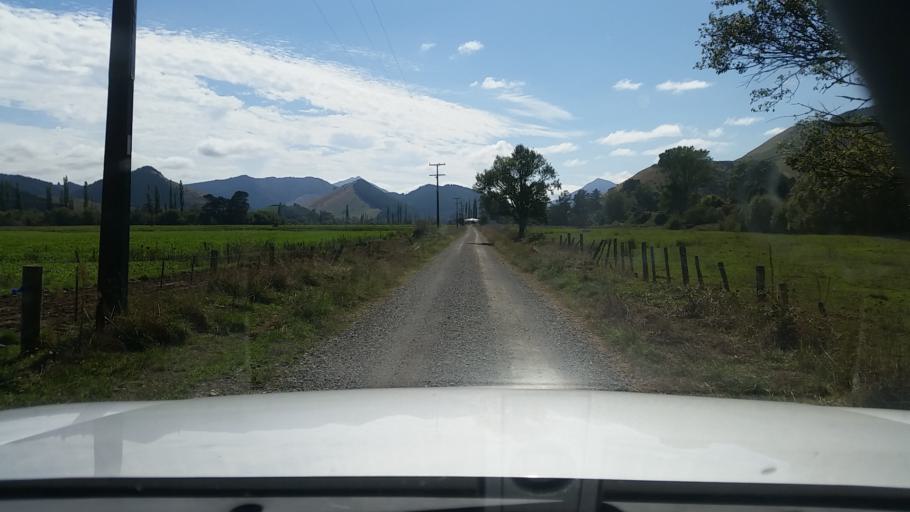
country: NZ
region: Nelson
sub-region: Nelson City
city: Nelson
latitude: -41.2536
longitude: 173.5826
